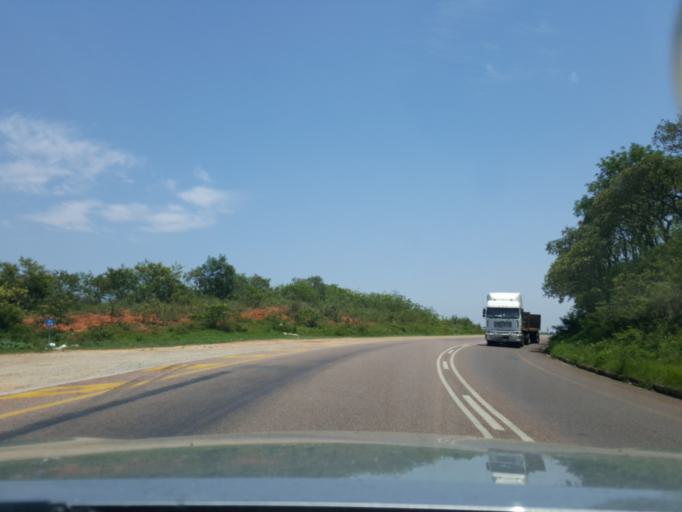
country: ZA
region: Limpopo
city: Thulamahashi
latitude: -24.8742
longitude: 31.1026
